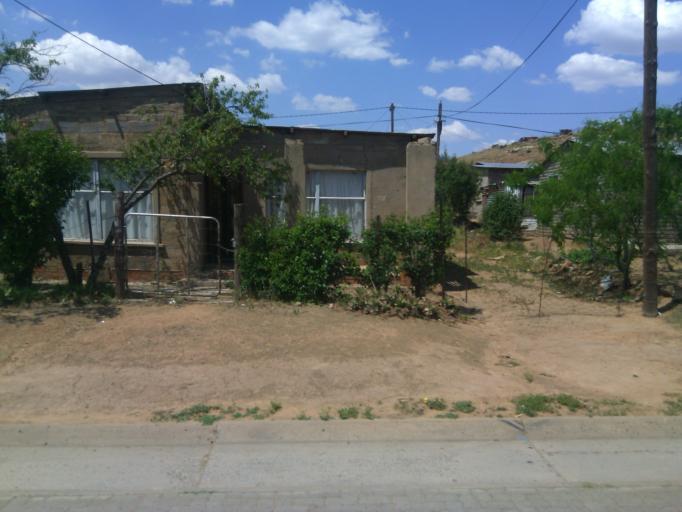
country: ZA
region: Orange Free State
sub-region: Xhariep District Municipality
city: Dewetsdorp
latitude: -29.5813
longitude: 26.6791
